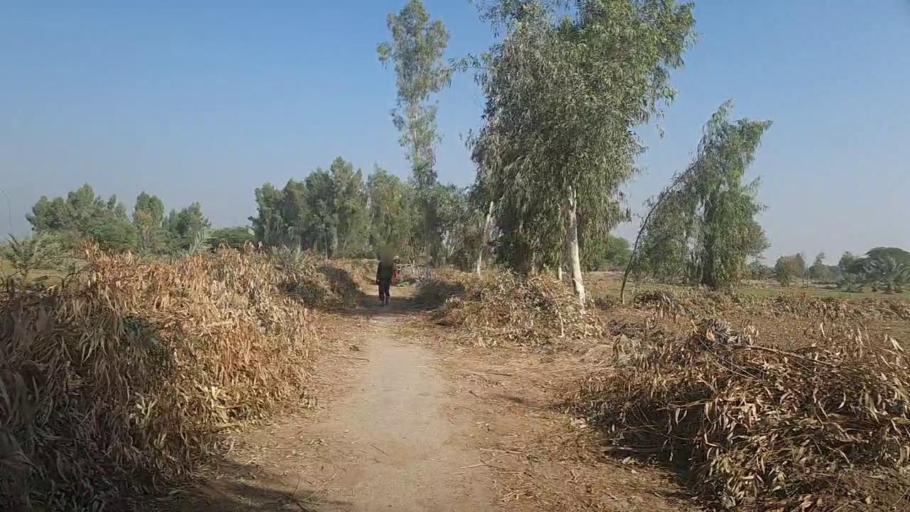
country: PK
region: Sindh
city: Kot Diji
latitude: 27.4313
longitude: 68.7323
